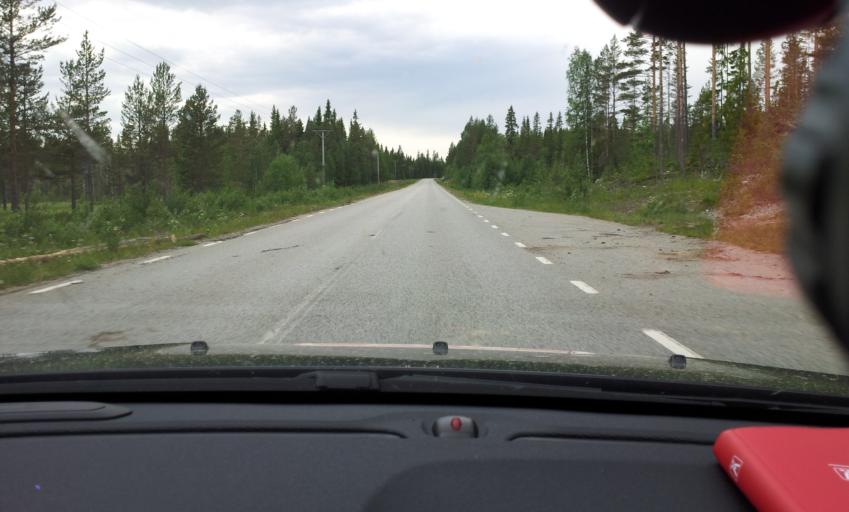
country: SE
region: Jaemtland
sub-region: Bergs Kommun
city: Hoverberg
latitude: 62.6755
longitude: 14.6850
